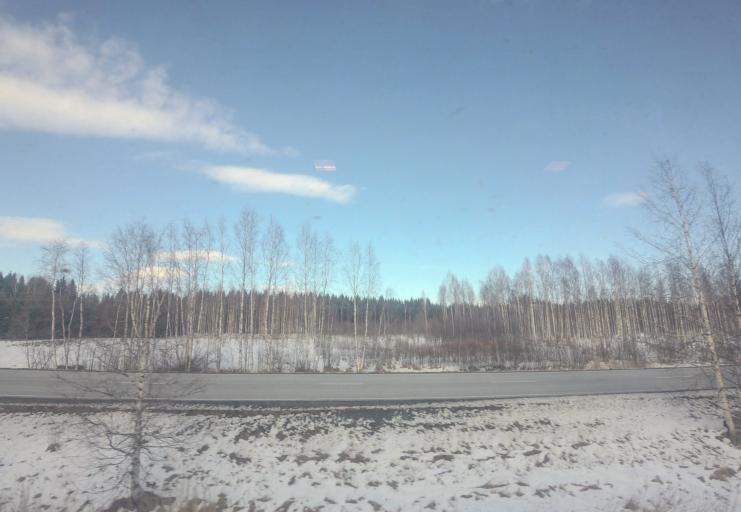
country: FI
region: Southern Savonia
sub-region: Savonlinna
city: Punkaharju
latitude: 61.7904
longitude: 29.3427
